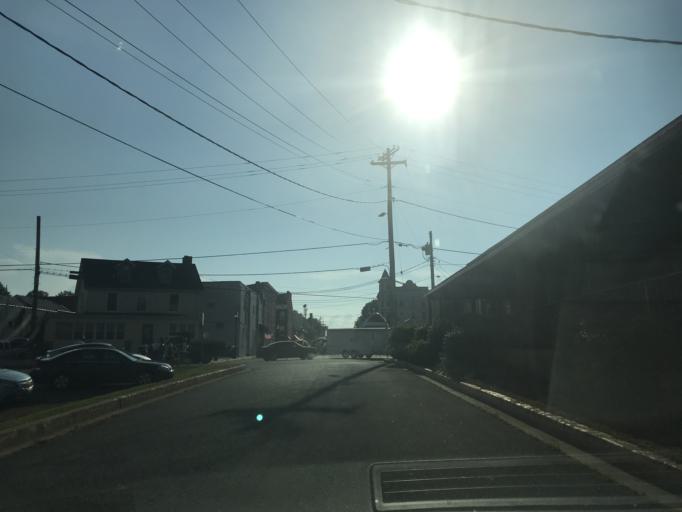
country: US
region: Maryland
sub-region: Harford County
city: Havre de Grace
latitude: 39.5488
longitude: -76.0884
